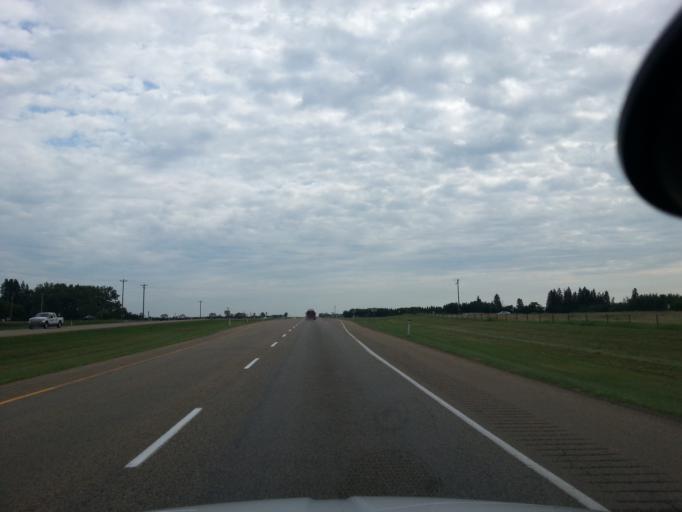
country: CA
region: Alberta
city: Sherwood Park
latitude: 53.5699
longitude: -113.2000
